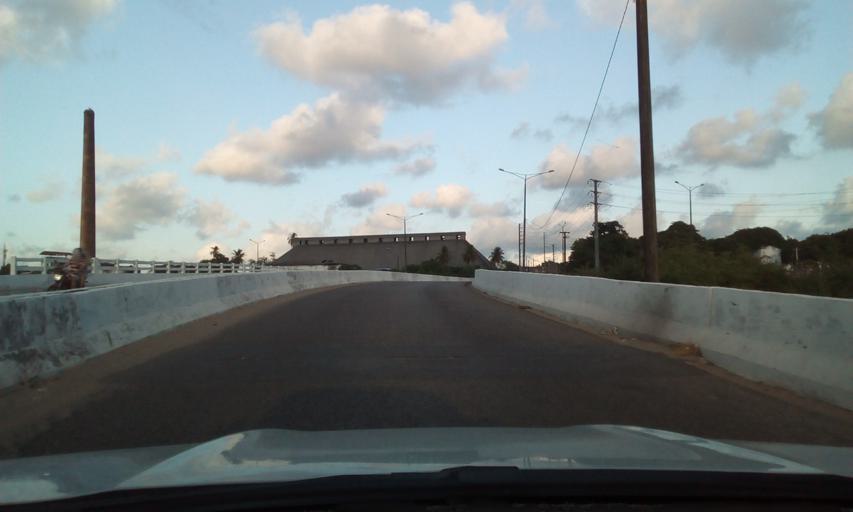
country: BR
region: Paraiba
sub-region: Joao Pessoa
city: Joao Pessoa
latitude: -7.1233
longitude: -34.8946
